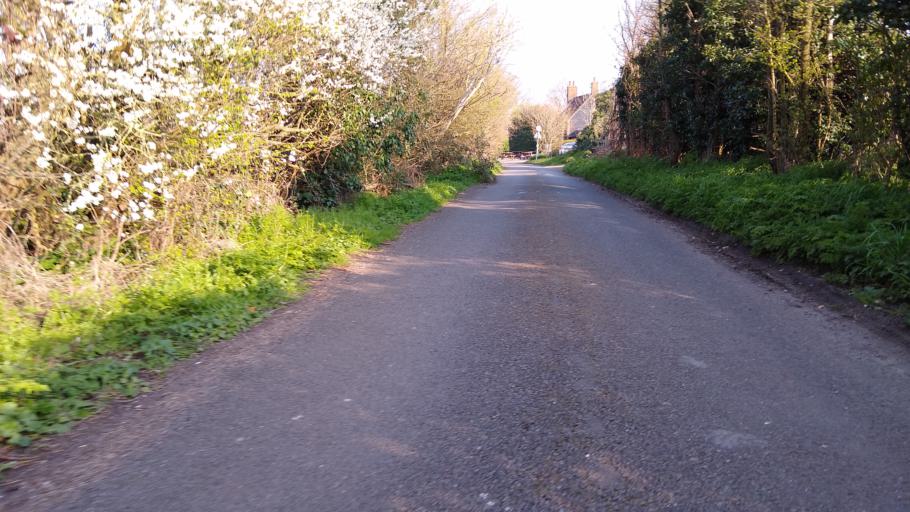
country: GB
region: England
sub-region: Wokingham
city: Winnersh
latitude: 51.4379
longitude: -0.8695
